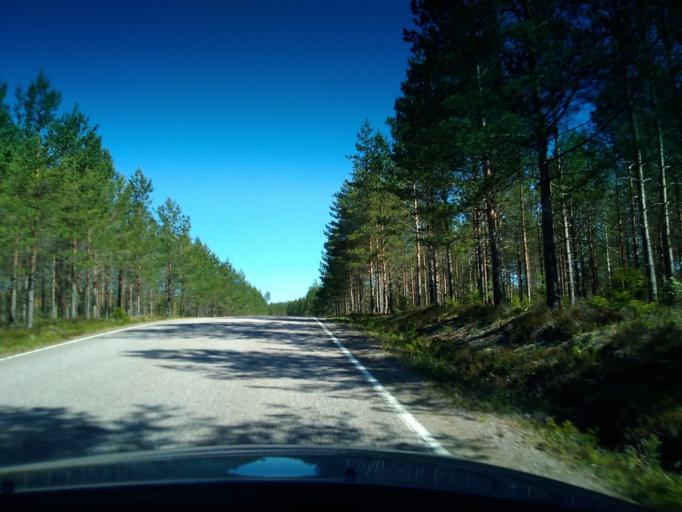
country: FI
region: Uusimaa
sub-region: Helsinki
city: Kaerkoelae
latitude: 60.6447
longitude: 23.9269
